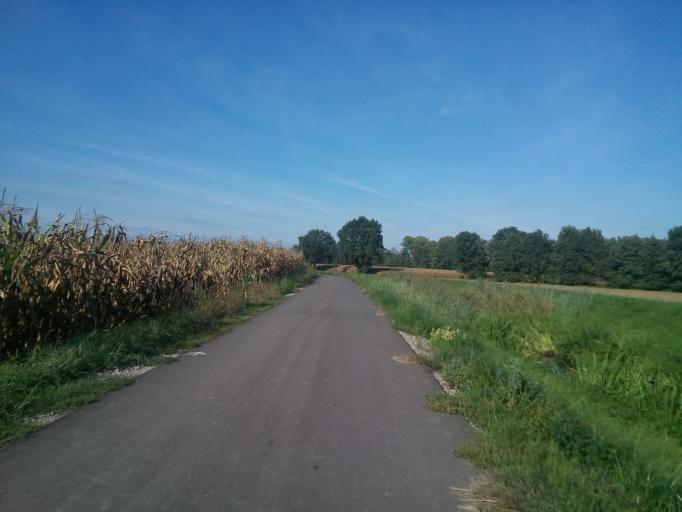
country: DE
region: Baden-Wuerttemberg
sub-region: Karlsruhe Region
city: Zell
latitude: 48.6704
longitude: 8.0716
